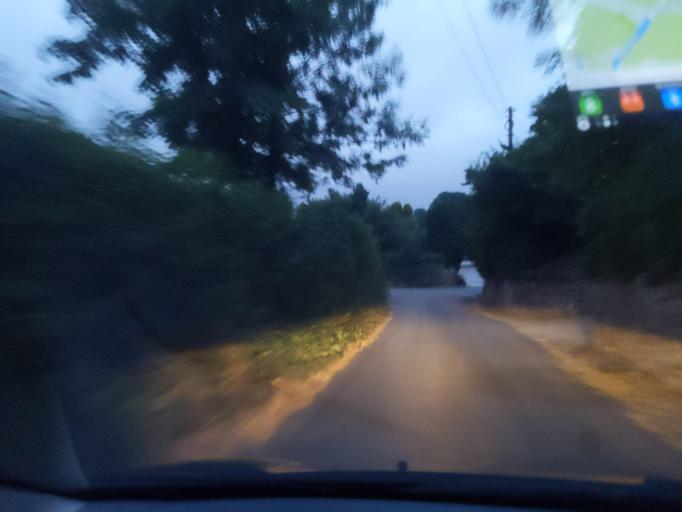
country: GB
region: England
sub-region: Devon
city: Ipplepen
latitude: 50.4823
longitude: -3.6454
